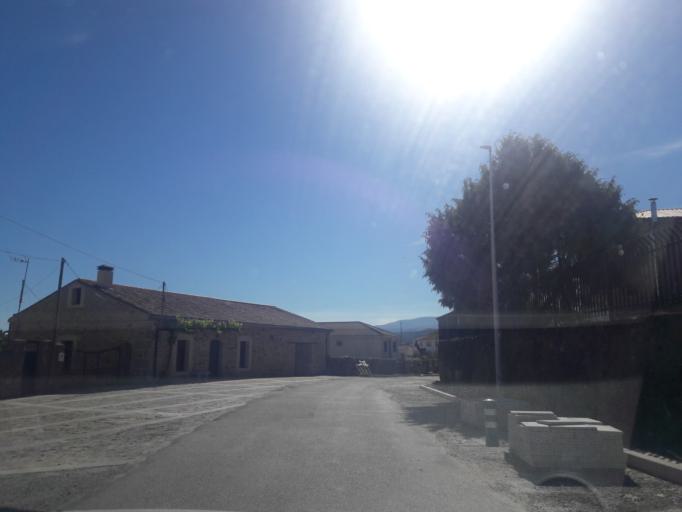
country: ES
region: Castille and Leon
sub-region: Provincia de Salamanca
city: Lagunilla
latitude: 40.3238
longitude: -5.9693
